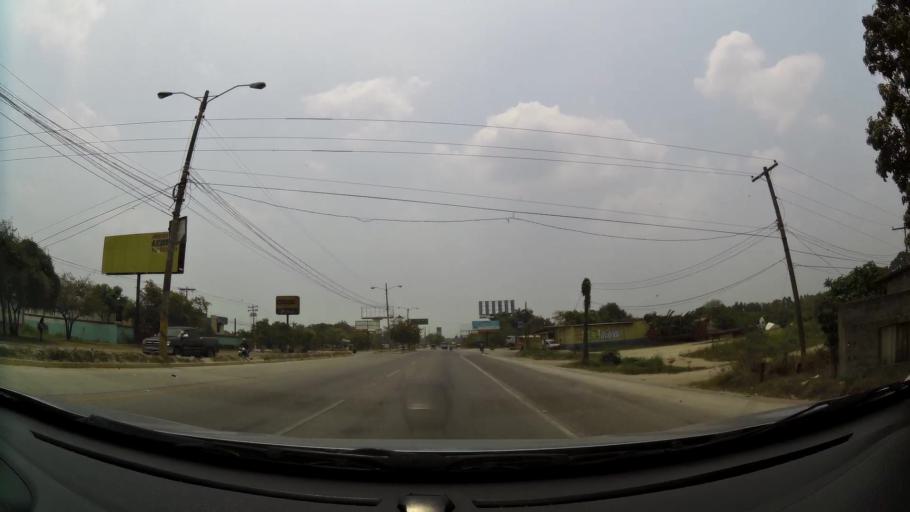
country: HN
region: Cortes
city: La Lima
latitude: 15.4566
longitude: -87.9518
